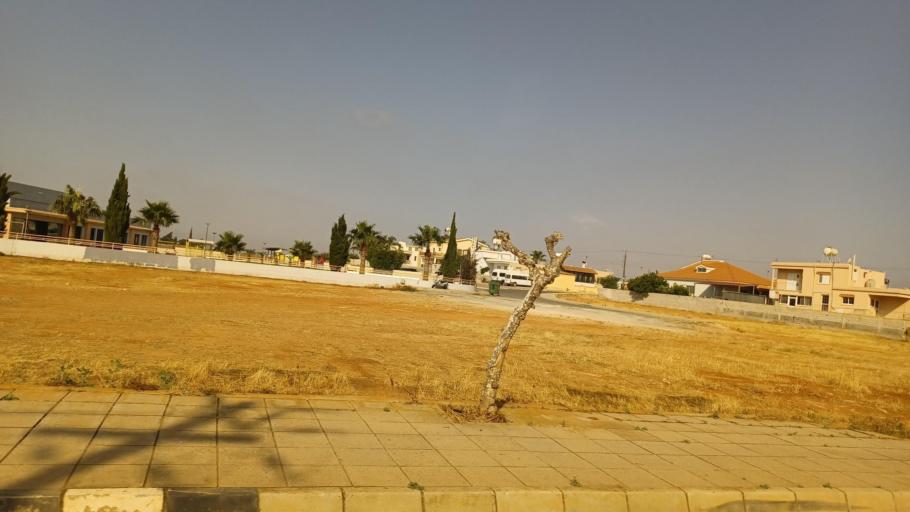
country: CY
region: Ammochostos
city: Avgorou
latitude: 35.0432
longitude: 33.8322
